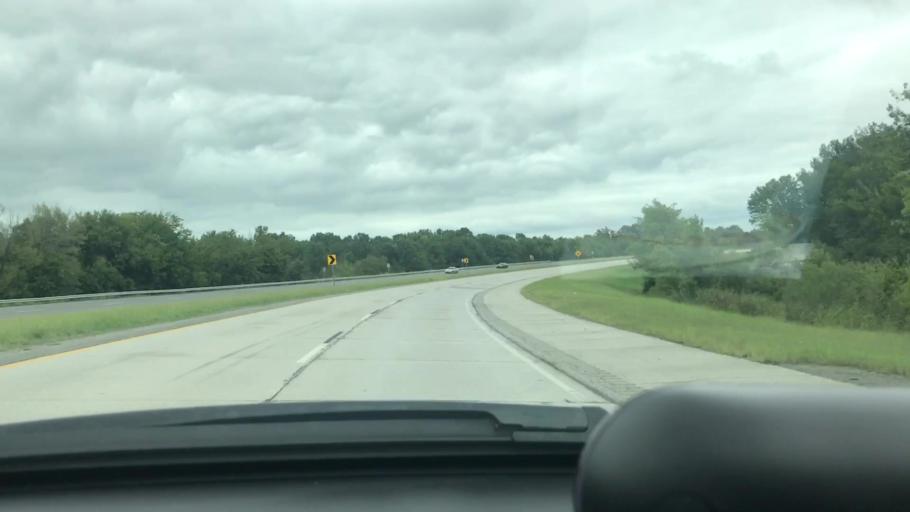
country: US
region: Oklahoma
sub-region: Wagoner County
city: Wagoner
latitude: 35.9110
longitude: -95.4024
